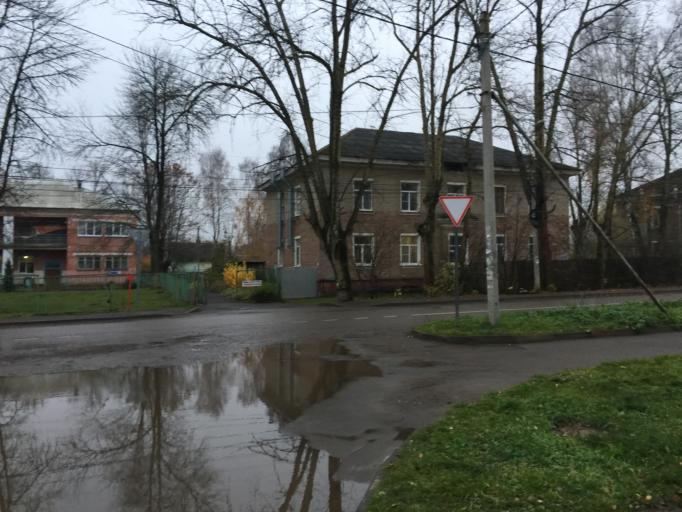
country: RU
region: Jaroslavl
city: Yaroslavl
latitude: 57.7198
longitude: 39.7747
